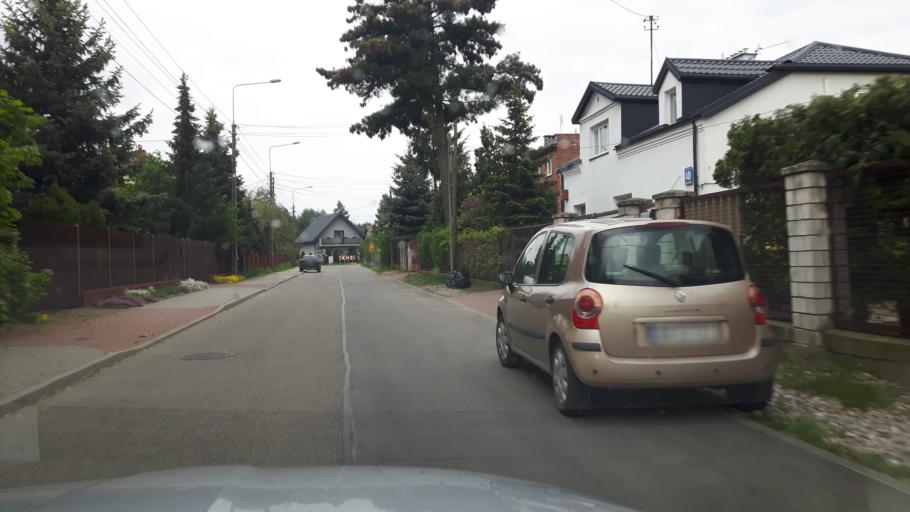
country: PL
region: Masovian Voivodeship
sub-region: Warszawa
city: Rembertow
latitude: 52.2498
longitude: 21.1695
